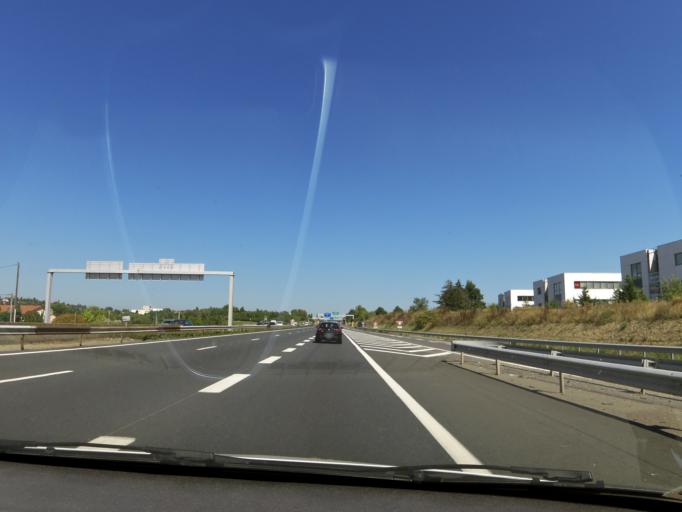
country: FR
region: Rhone-Alpes
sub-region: Departement du Rhone
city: Dardilly
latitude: 45.8109
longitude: 4.7682
